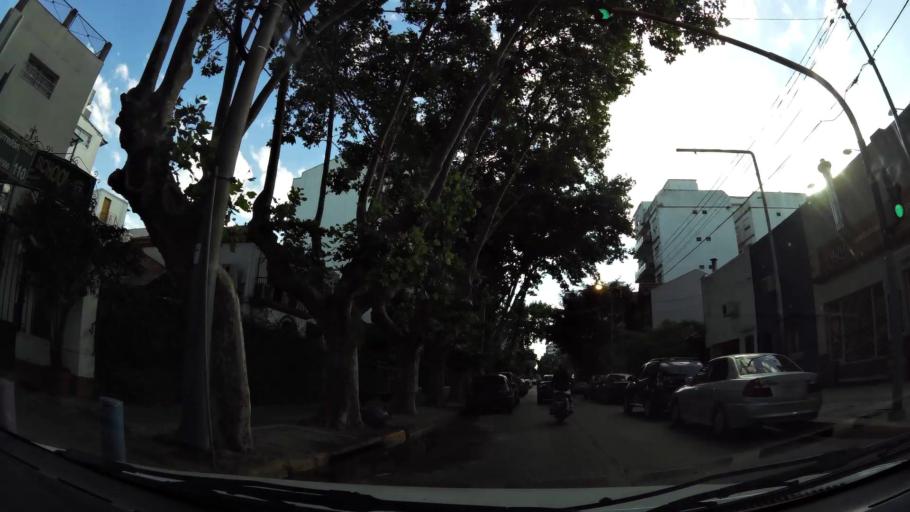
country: AR
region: Buenos Aires
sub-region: Partido de General San Martin
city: General San Martin
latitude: -34.5485
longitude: -58.5502
